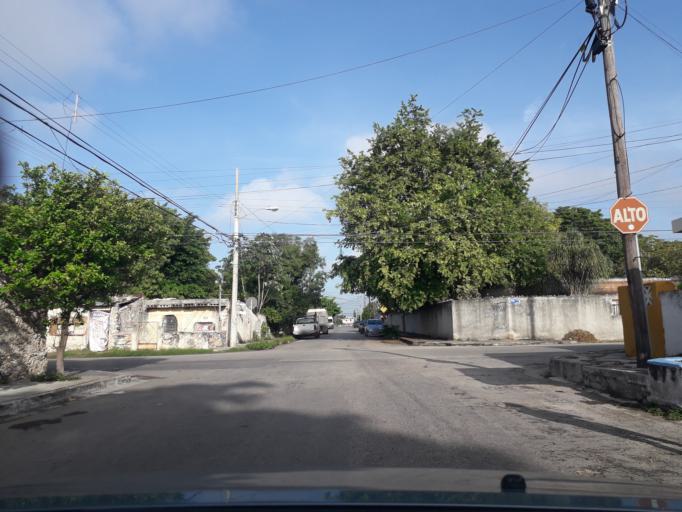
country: MX
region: Yucatan
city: Merida
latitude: 20.9786
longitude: -89.6540
